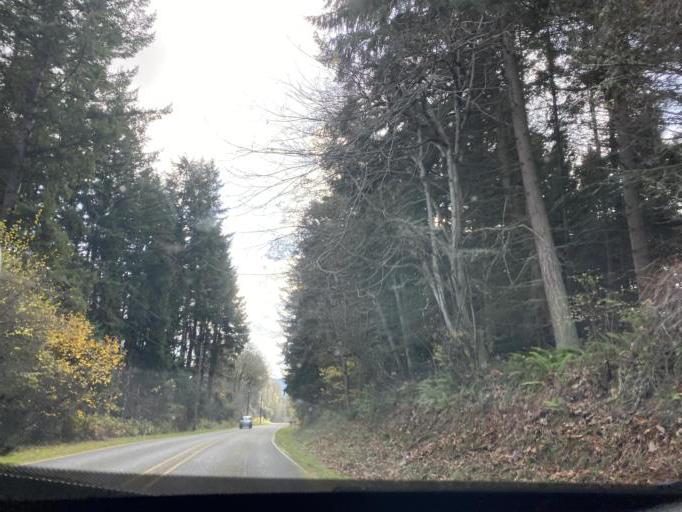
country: US
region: Washington
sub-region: Island County
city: Langley
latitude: 47.9610
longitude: -122.4424
